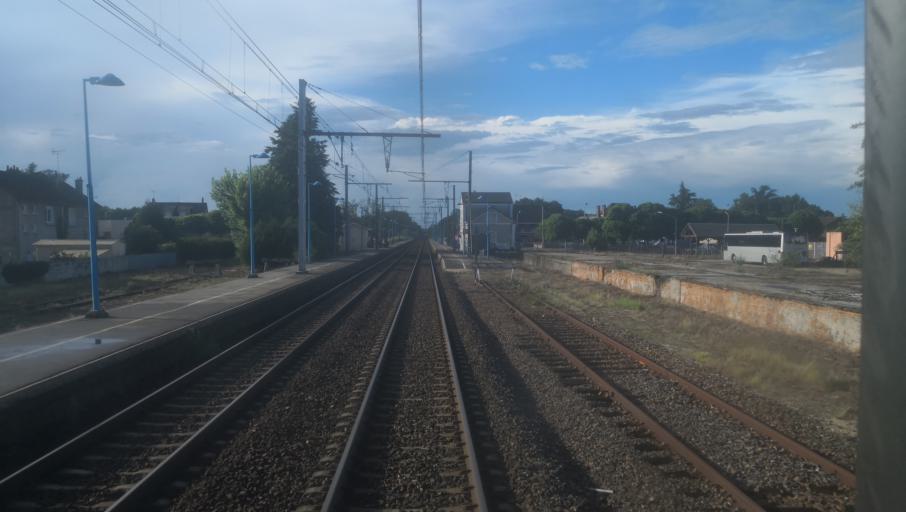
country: FR
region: Centre
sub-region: Departement du Loir-et-Cher
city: Salbris
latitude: 47.4239
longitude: 2.0479
